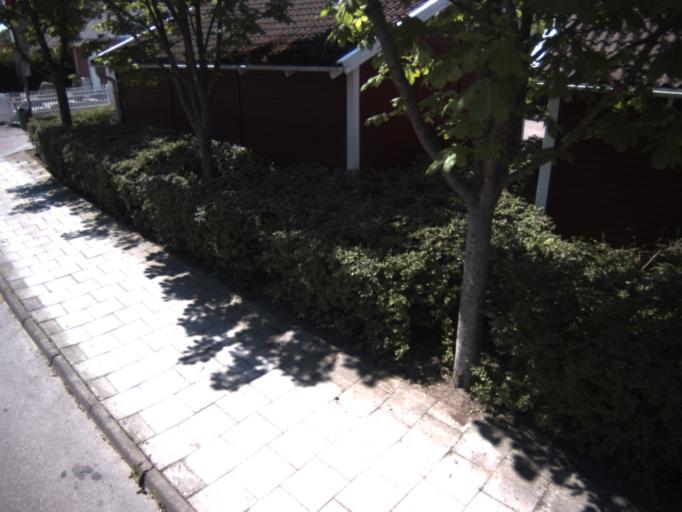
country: SE
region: Skane
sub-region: Helsingborg
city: Rydeback
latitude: 56.0047
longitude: 12.7615
